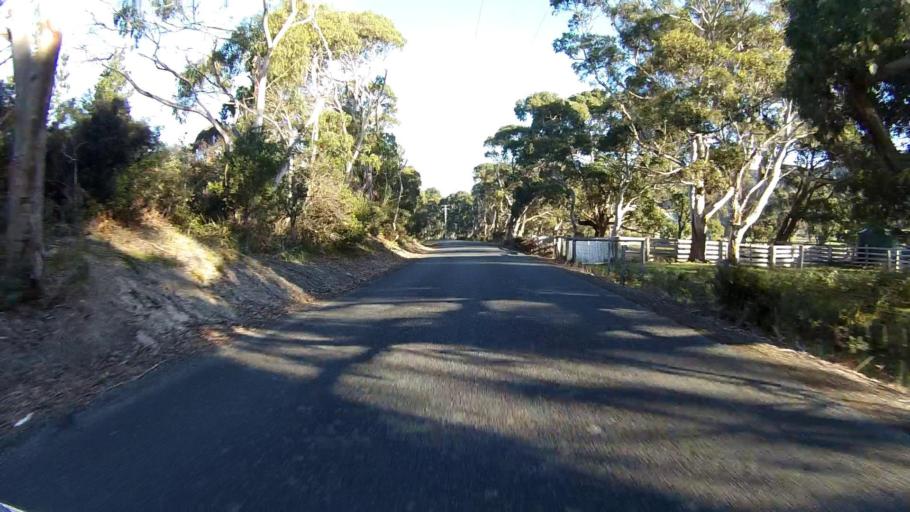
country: AU
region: Tasmania
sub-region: Clarence
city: Sandford
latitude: -43.1761
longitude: 147.8538
